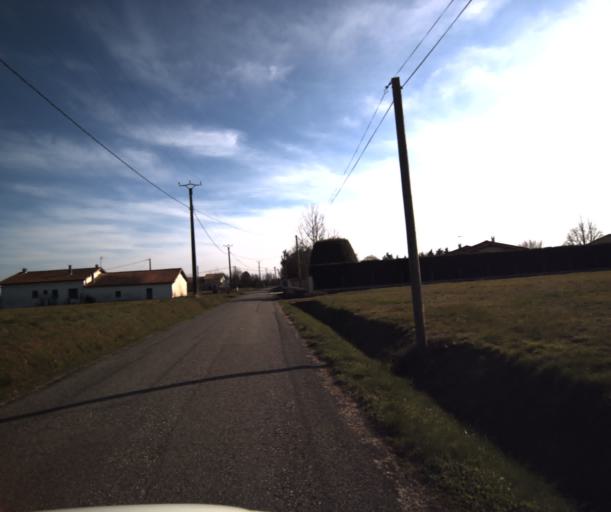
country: FR
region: Midi-Pyrenees
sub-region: Departement du Tarn-et-Garonne
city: Labastide-Saint-Pierre
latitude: 43.9273
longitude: 1.3438
